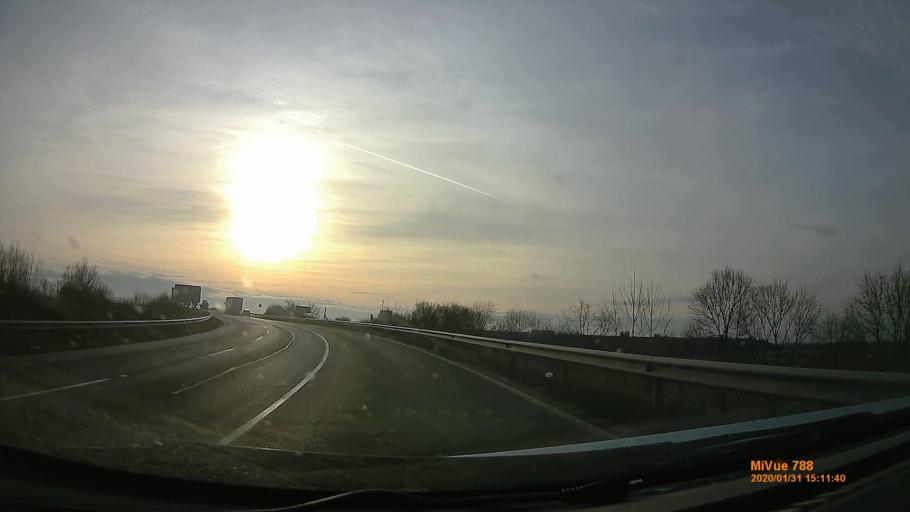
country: HU
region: Hajdu-Bihar
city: Polgar
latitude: 47.8483
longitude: 21.1486
